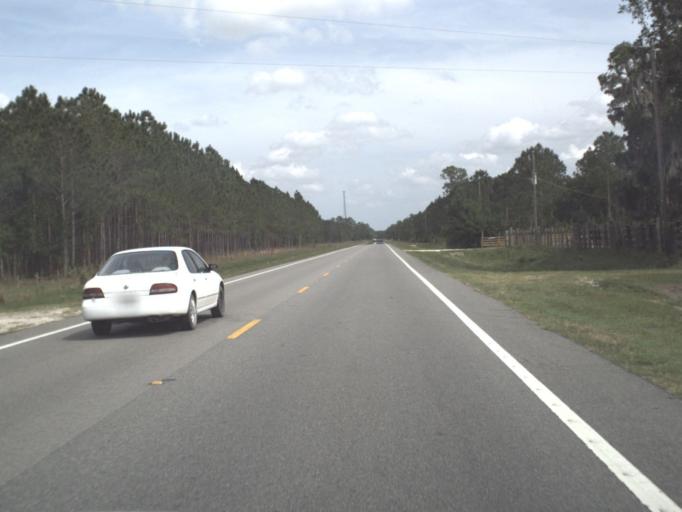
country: US
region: Florida
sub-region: Putnam County
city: Crescent City
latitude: 29.4910
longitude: -81.4725
